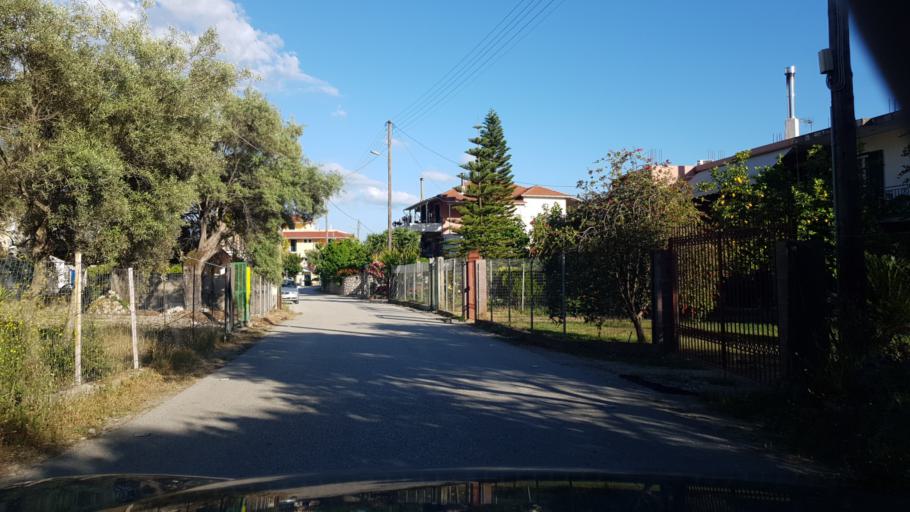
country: GR
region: Ionian Islands
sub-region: Lefkada
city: Nidri
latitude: 38.7117
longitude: 20.7042
